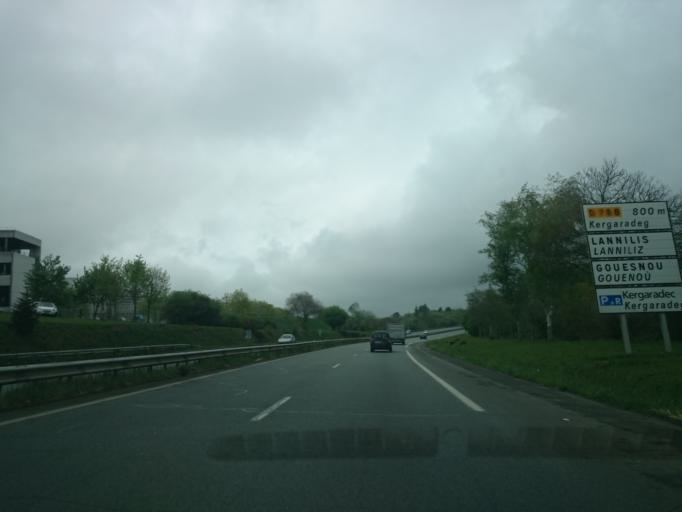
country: FR
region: Brittany
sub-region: Departement du Finistere
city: Gouesnou
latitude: 48.4282
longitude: -4.4747
